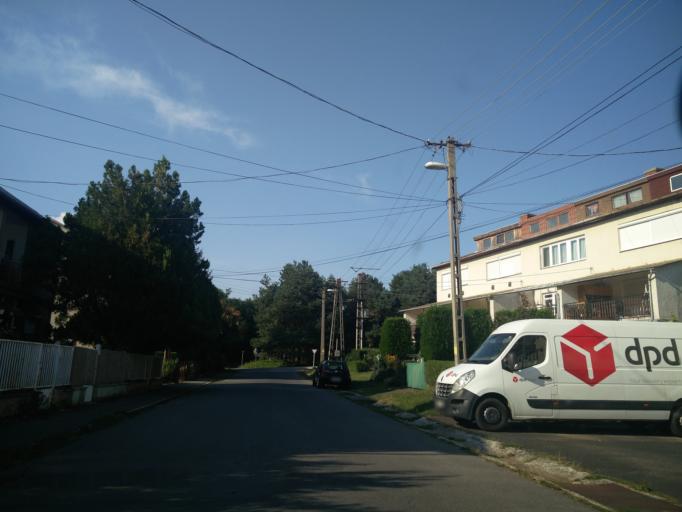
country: HU
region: Zala
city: Zalaegerszeg
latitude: 46.8662
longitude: 16.8024
